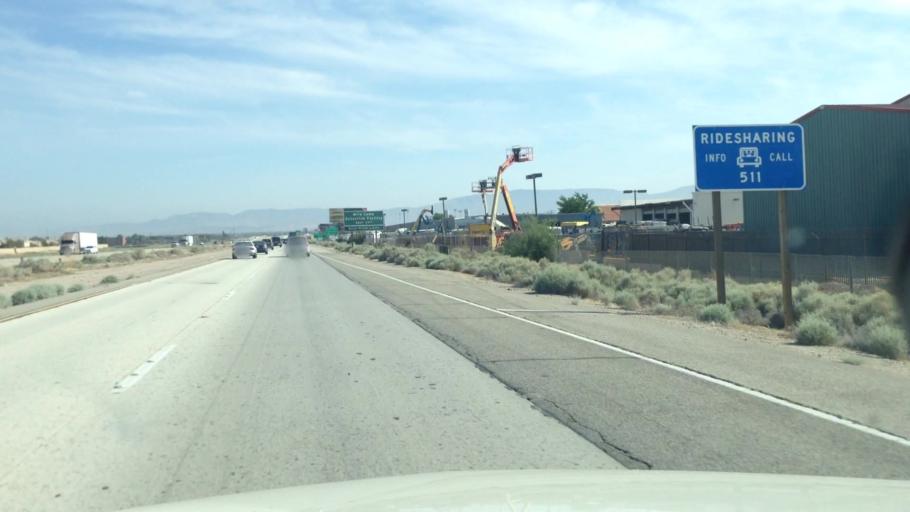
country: US
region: California
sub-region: Los Angeles County
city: Lancaster
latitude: 34.7147
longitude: -118.1704
